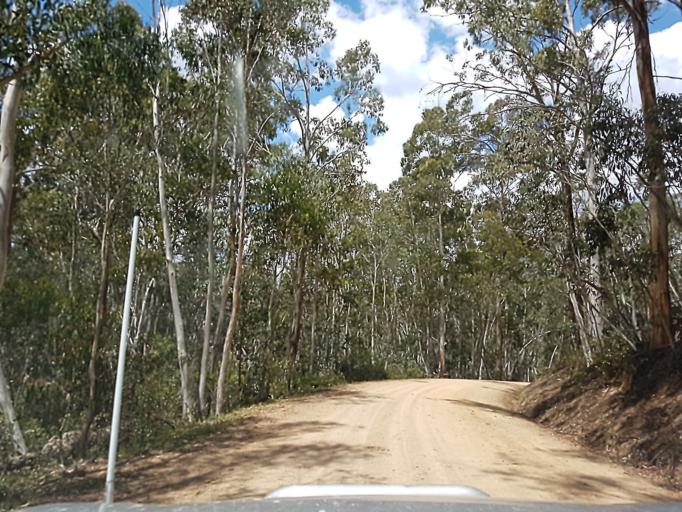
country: AU
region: New South Wales
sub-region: Snowy River
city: Jindabyne
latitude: -36.8854
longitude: 148.0838
